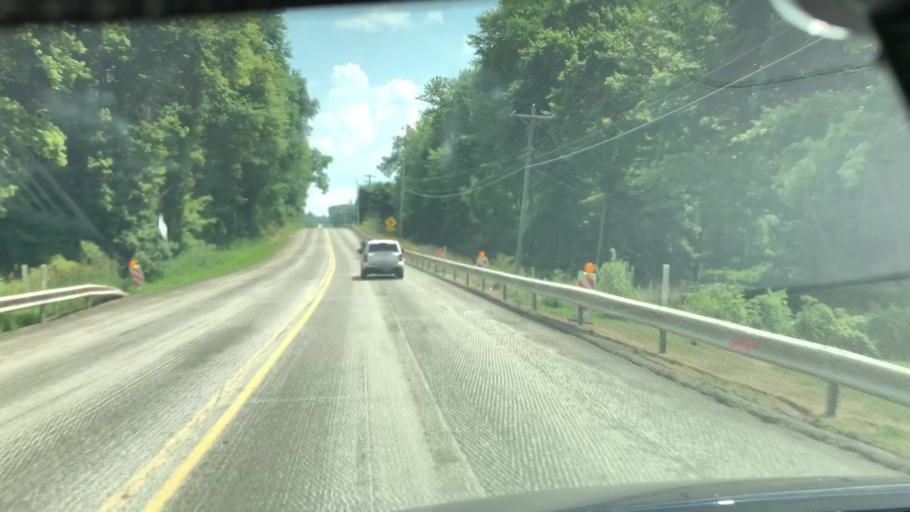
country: US
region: Pennsylvania
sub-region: Butler County
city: Saxonburg
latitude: 40.7964
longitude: -79.8190
